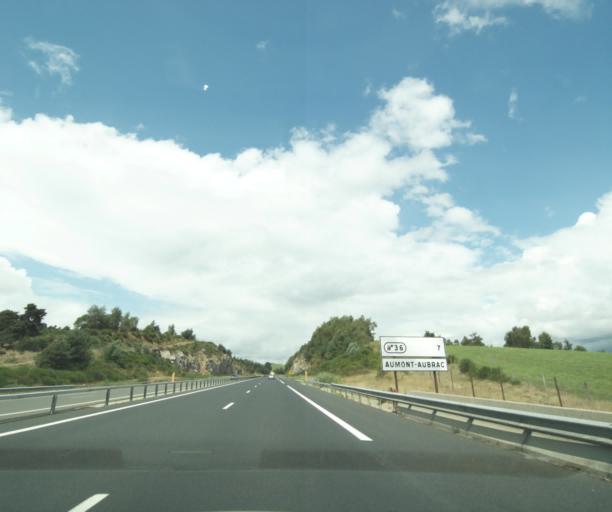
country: FR
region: Languedoc-Roussillon
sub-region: Departement de la Lozere
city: Aumont-Aubrac
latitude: 44.6415
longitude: 3.2425
